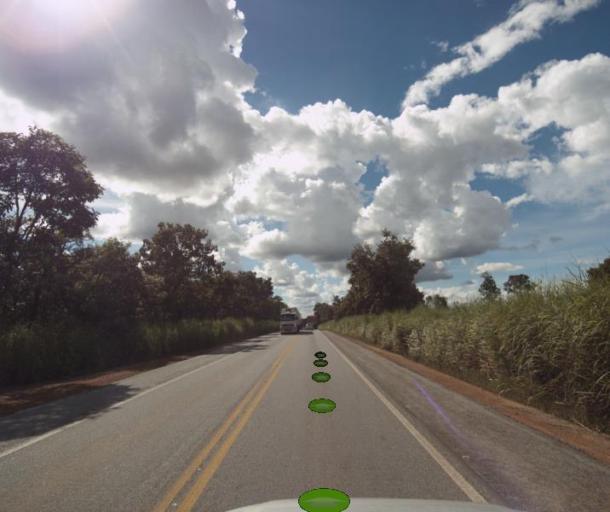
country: BR
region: Goias
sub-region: Porangatu
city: Porangatu
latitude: -13.2095
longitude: -49.1533
